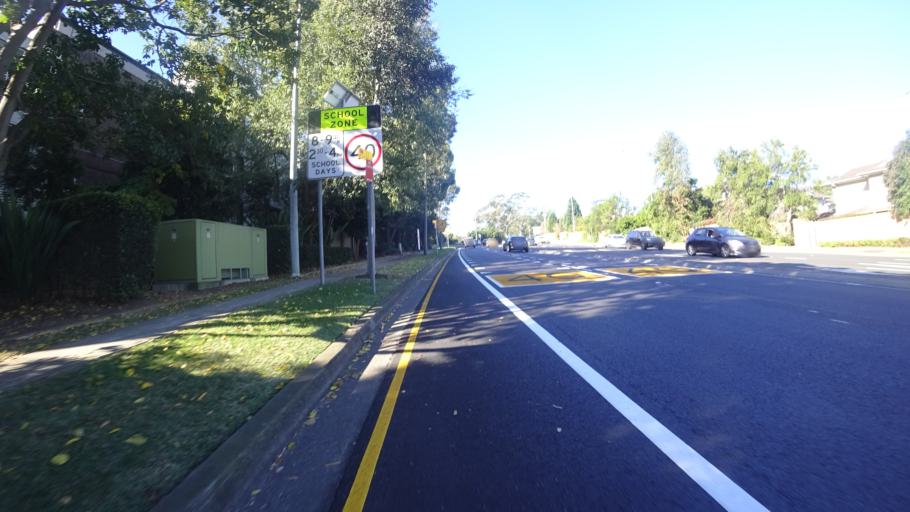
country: AU
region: New South Wales
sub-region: The Hills Shire
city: Castle Hill
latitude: -33.7311
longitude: 151.0105
